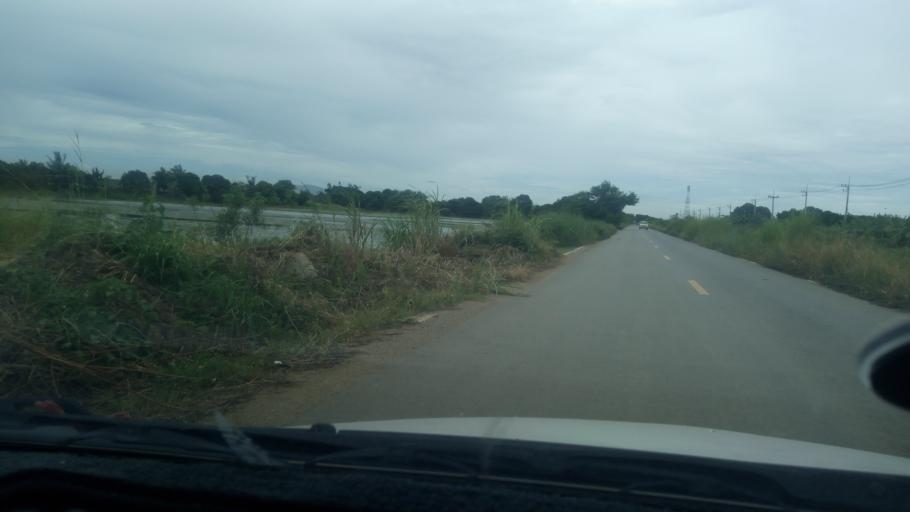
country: TH
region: Chon Buri
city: Phanat Nikhom
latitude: 13.5313
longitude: 101.1587
